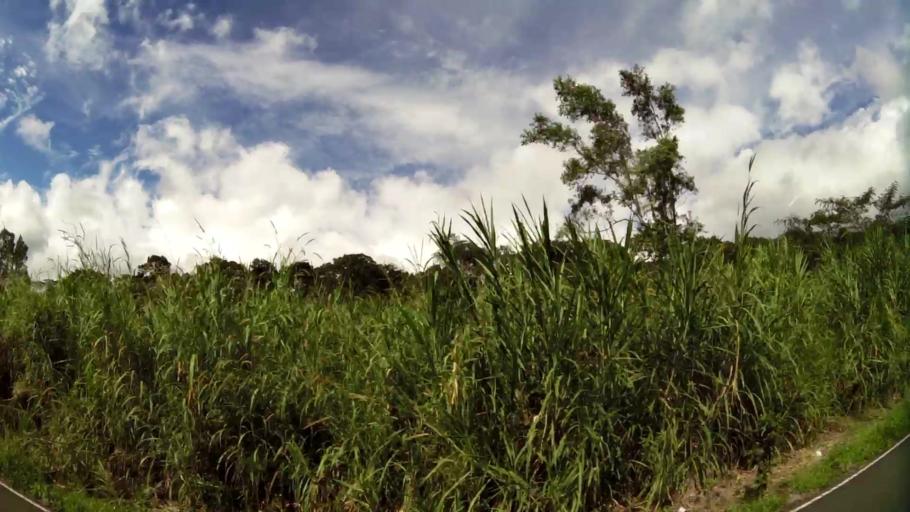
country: PA
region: Chiriqui
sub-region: Distrito Boquete
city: Boquete
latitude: 8.7919
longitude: -82.4286
